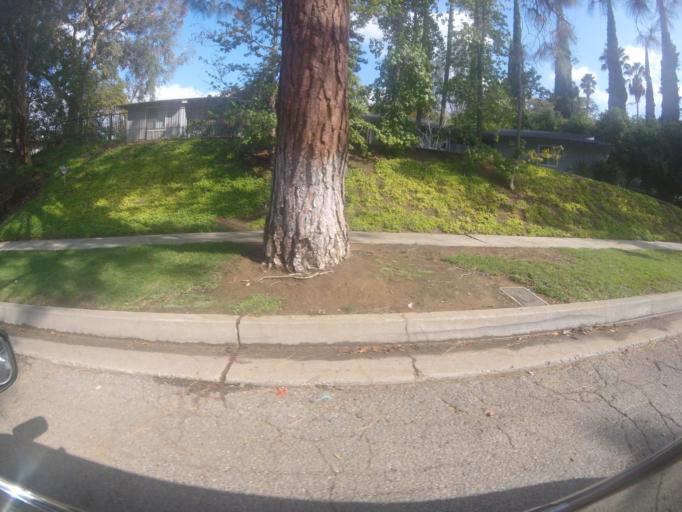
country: US
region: California
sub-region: San Bernardino County
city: Redlands
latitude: 34.0316
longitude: -117.1765
